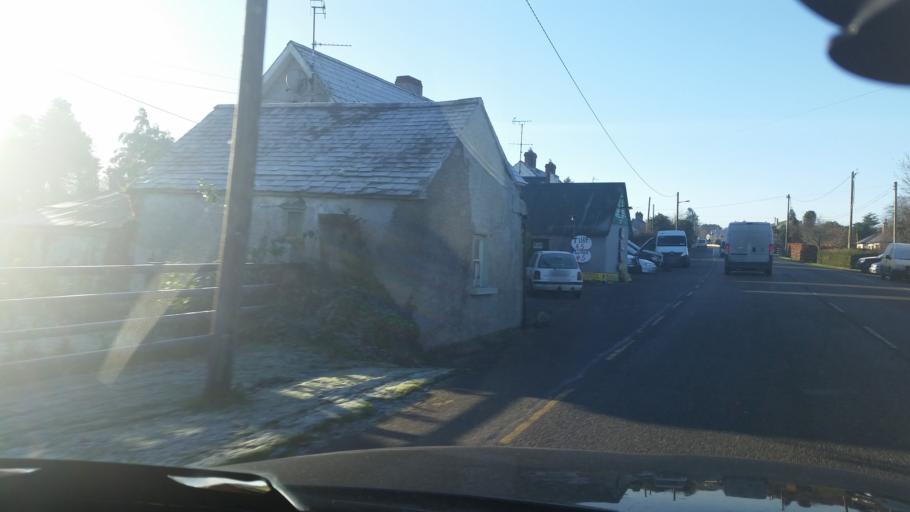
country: IE
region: Leinster
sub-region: Loch Garman
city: Ballinroad
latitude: 52.5442
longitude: -6.3399
